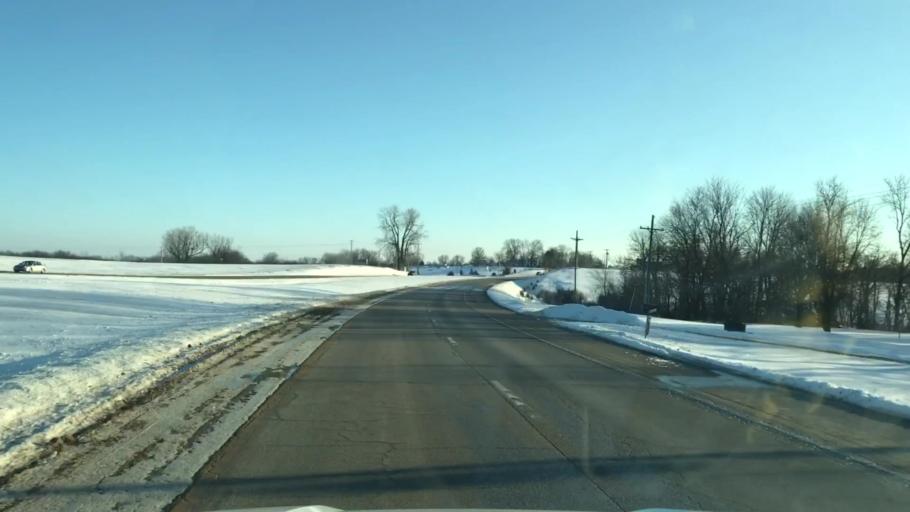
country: US
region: Missouri
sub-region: Andrew County
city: Country Club Village
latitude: 39.8855
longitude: -94.8087
